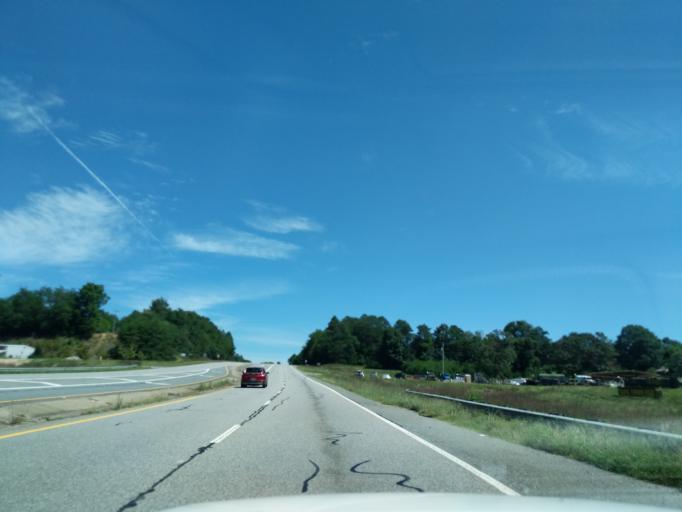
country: US
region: Georgia
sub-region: Fannin County
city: Blue Ridge
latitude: 34.8890
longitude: -84.2231
